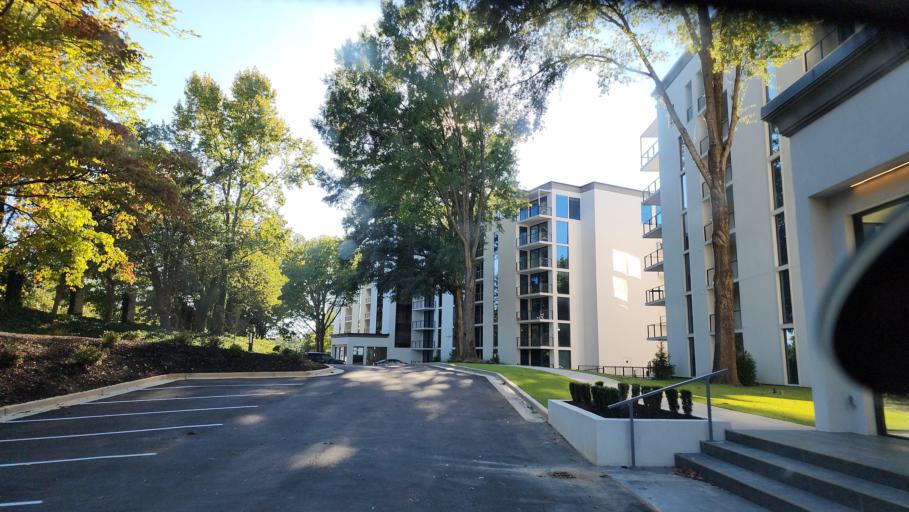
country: US
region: Georgia
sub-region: Cobb County
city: Vinings
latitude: 33.9075
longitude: -84.4674
